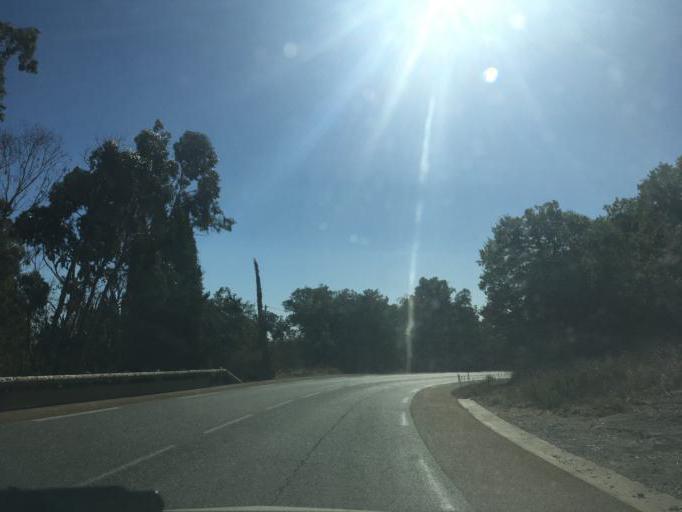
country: FR
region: Provence-Alpes-Cote d'Azur
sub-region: Departement du Var
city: La Garde-Freinet
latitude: 43.2992
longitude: 6.4921
